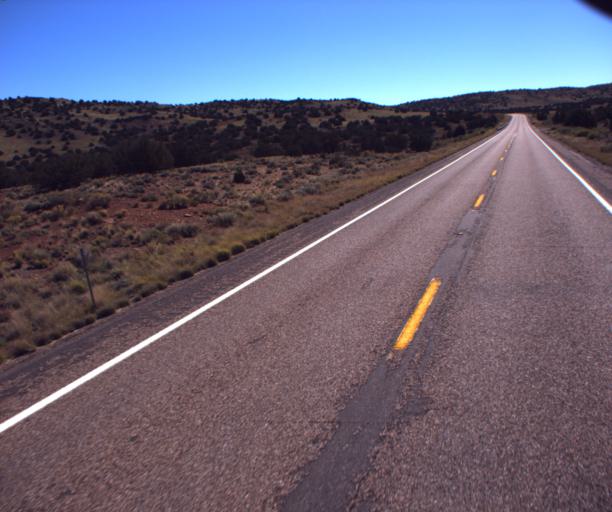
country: US
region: Arizona
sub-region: Apache County
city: Saint Johns
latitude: 34.5780
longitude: -109.5329
